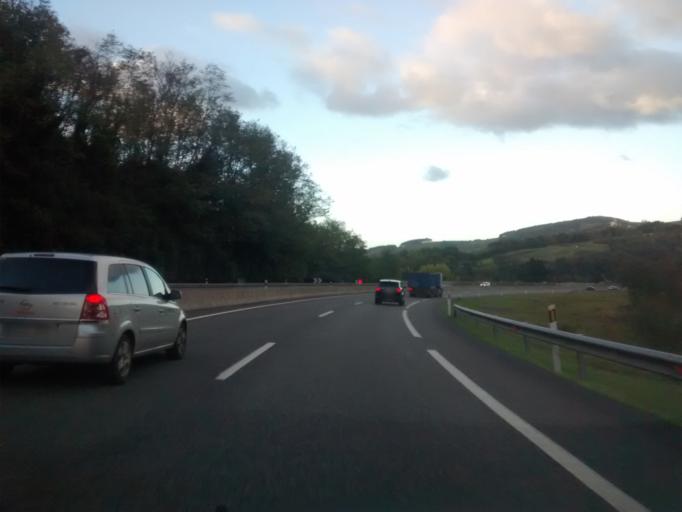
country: ES
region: Basque Country
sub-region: Provincia de Guipuzcoa
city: Zumaia
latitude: 43.2758
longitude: -2.2551
